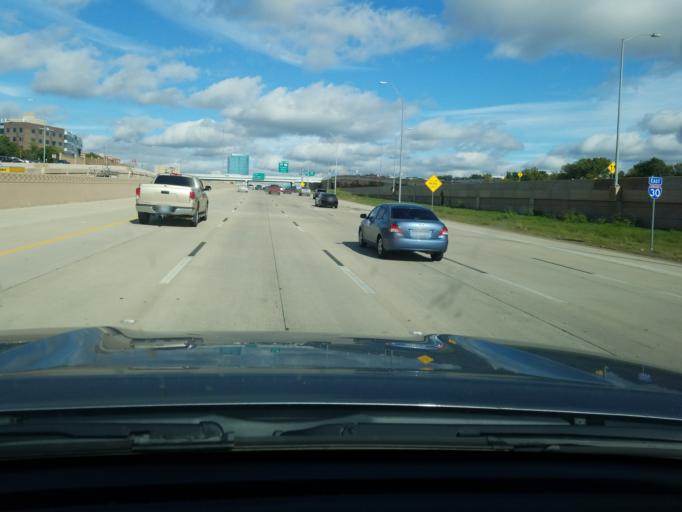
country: US
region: Texas
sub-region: Tarrant County
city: Fort Worth
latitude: 32.7409
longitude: -97.3451
